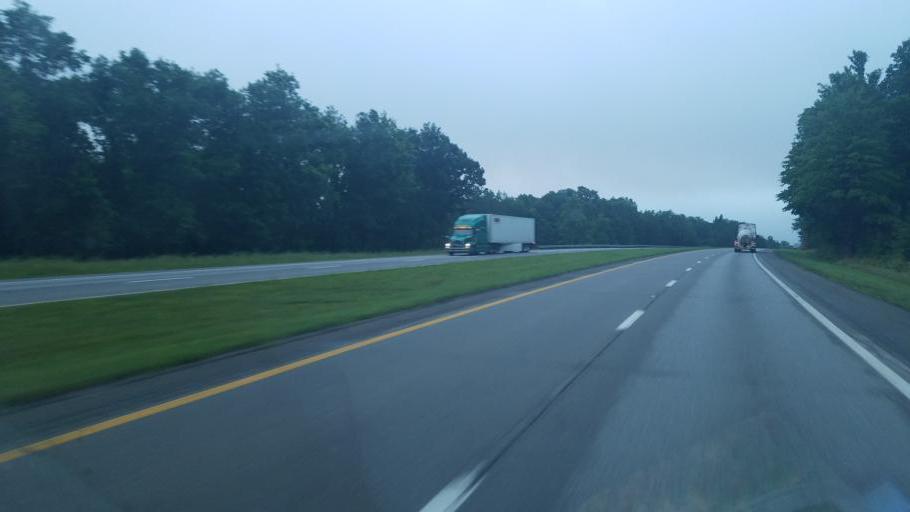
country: US
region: Ohio
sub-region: Jackson County
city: Jackson
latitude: 39.0215
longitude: -82.5797
